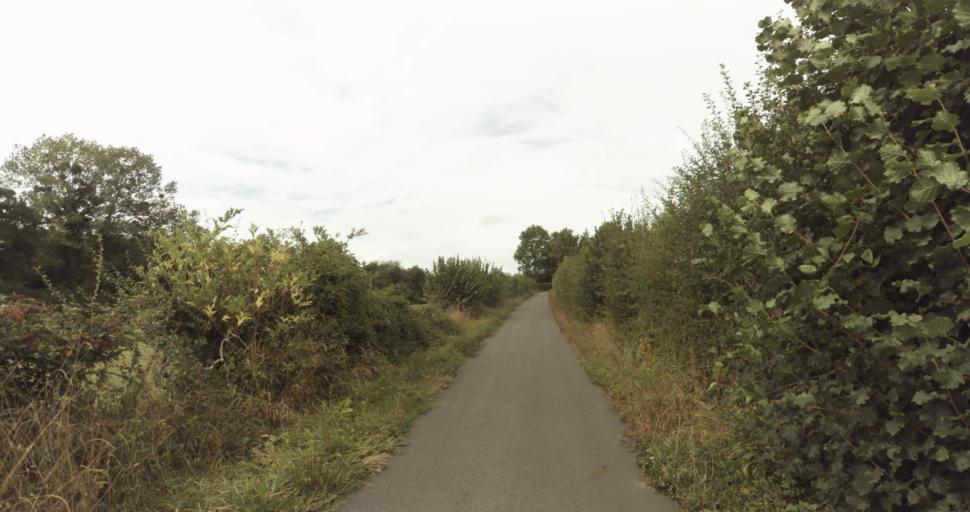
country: FR
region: Lower Normandy
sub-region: Departement de l'Orne
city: Gace
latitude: 48.8141
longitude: 0.2870
